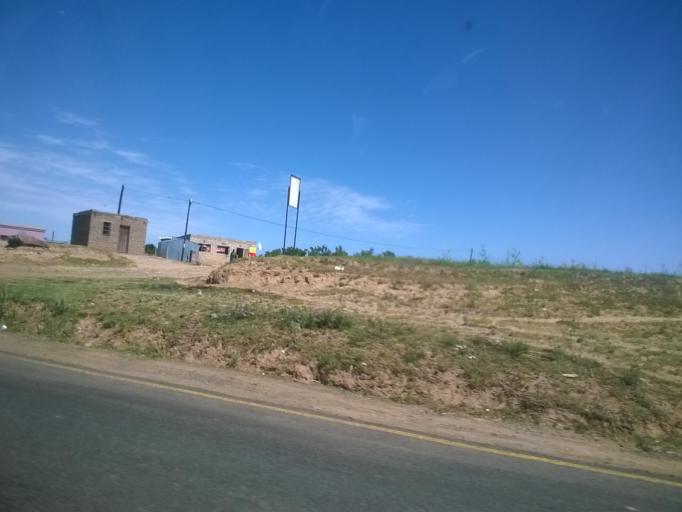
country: LS
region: Berea
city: Teyateyaneng
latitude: -29.0919
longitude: 27.9370
